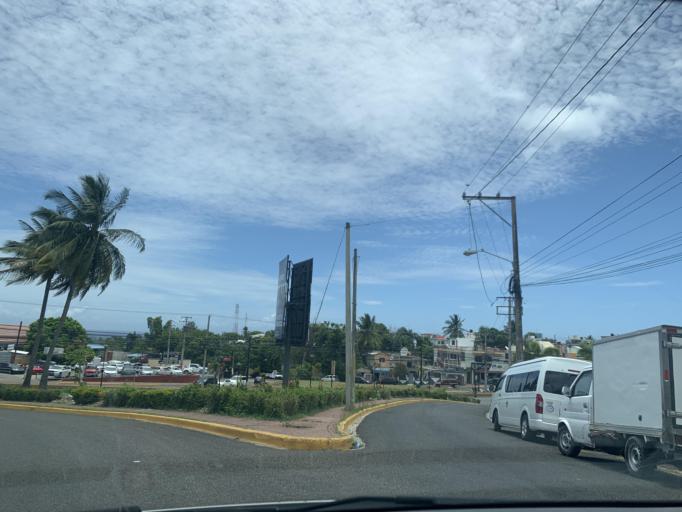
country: DO
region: Puerto Plata
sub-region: Puerto Plata
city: Puerto Plata
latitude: 19.7863
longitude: -70.6910
